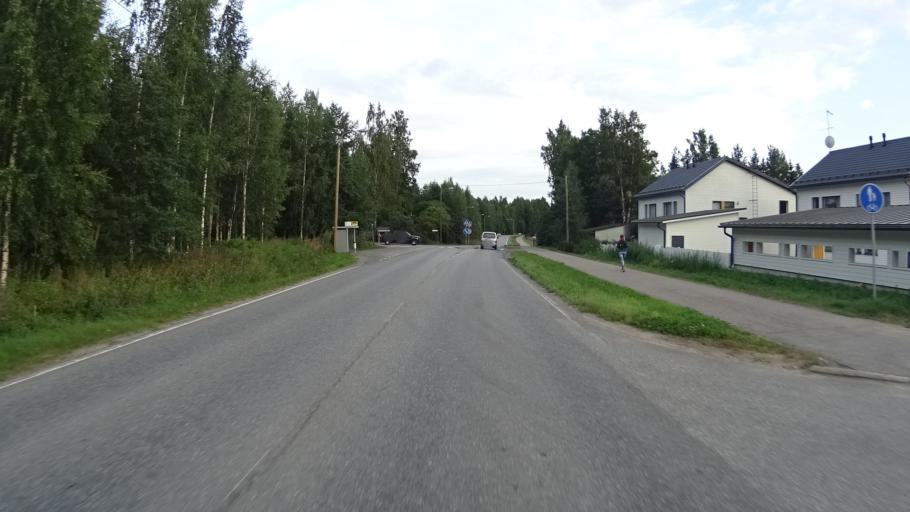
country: FI
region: Uusimaa
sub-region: Helsinki
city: Kilo
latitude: 60.3264
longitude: 24.8666
